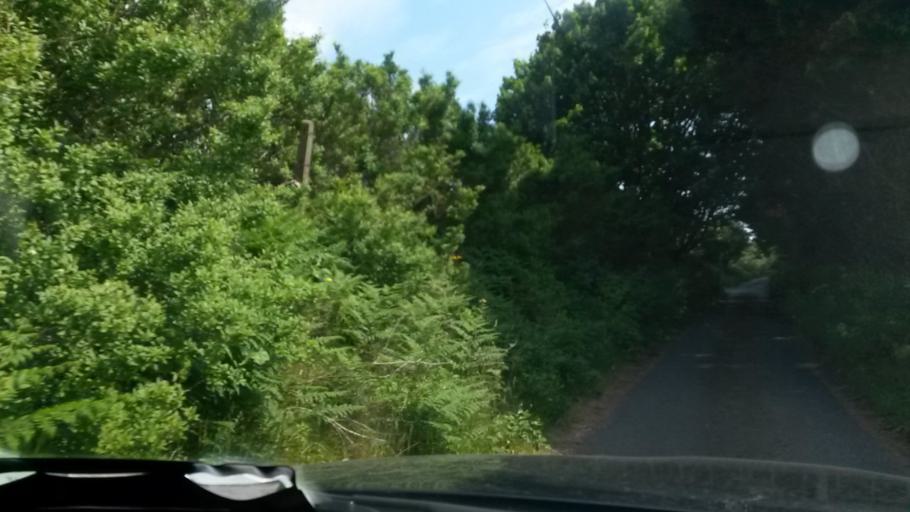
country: IE
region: Leinster
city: Portraine
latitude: 53.5080
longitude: -6.1269
